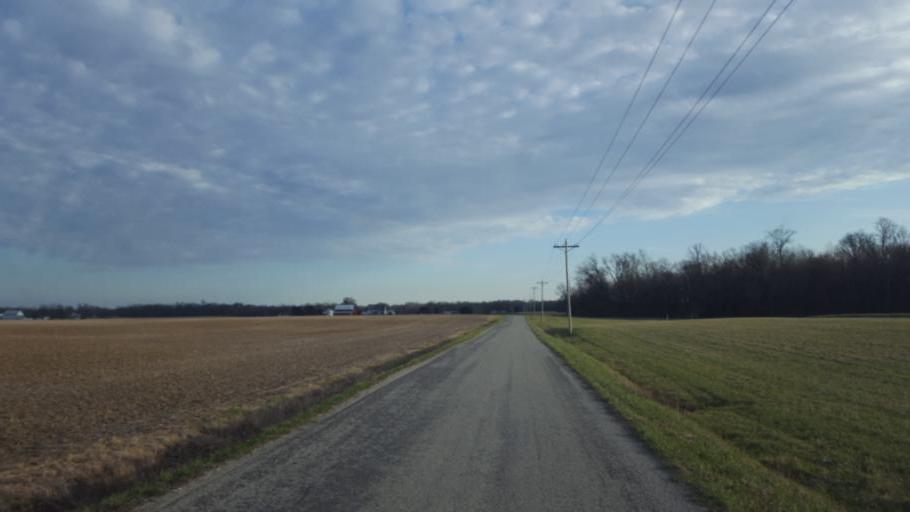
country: US
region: Ohio
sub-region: Marion County
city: Marion
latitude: 40.6089
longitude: -82.9910
